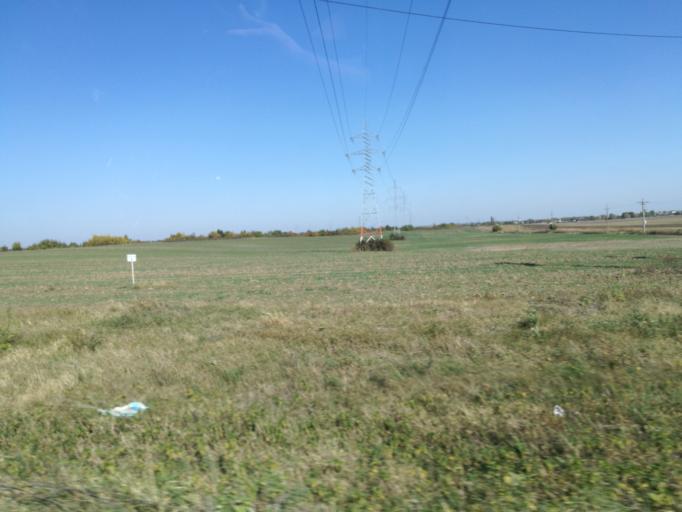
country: RO
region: Ilfov
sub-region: Comuna Dragomiresti-Vale
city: Dragomiresti-Vale
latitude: 44.4734
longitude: 25.9117
